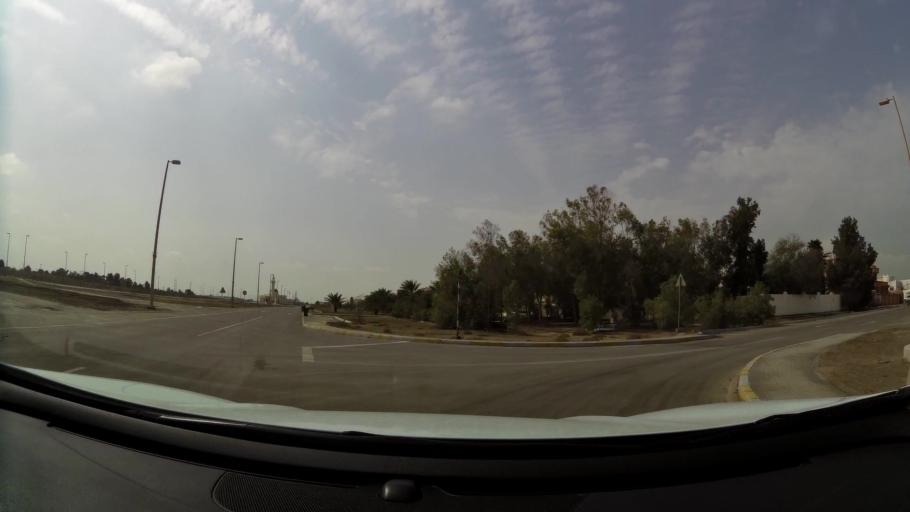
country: AE
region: Abu Dhabi
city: Abu Dhabi
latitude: 24.5523
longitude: 54.6390
